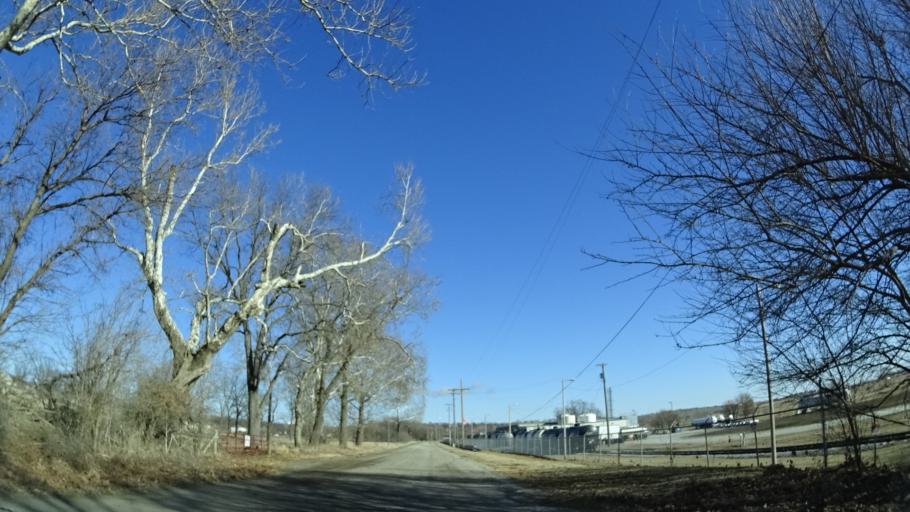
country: US
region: Nebraska
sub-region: Sarpy County
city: Offutt Air Force Base
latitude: 41.1470
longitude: -95.9526
